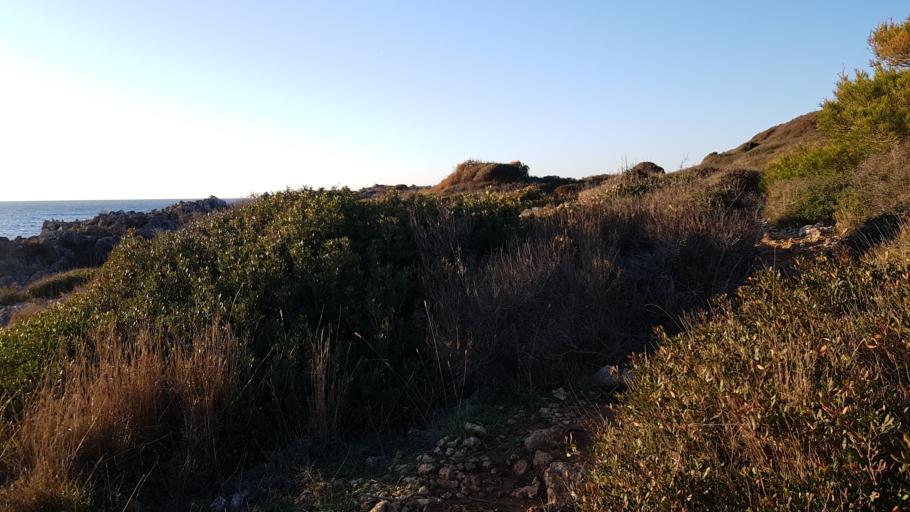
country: IT
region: Apulia
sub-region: Provincia di Lecce
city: Nardo
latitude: 40.1526
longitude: 17.9618
